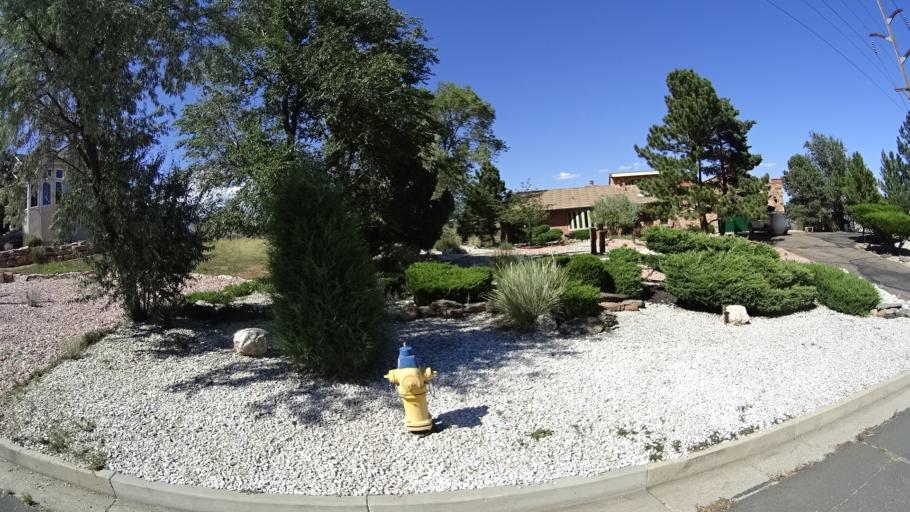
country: US
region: Colorado
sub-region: El Paso County
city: Colorado Springs
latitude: 38.8621
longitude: -104.8466
